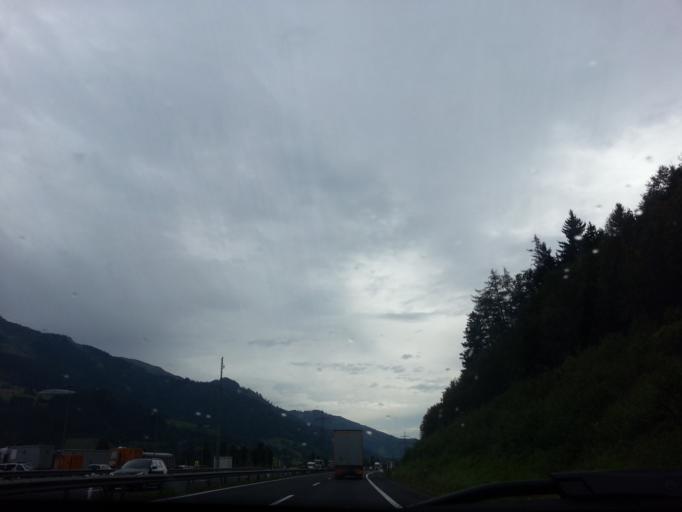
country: AT
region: Styria
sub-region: Politischer Bezirk Liezen
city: Treglwang
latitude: 47.4795
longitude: 14.5605
